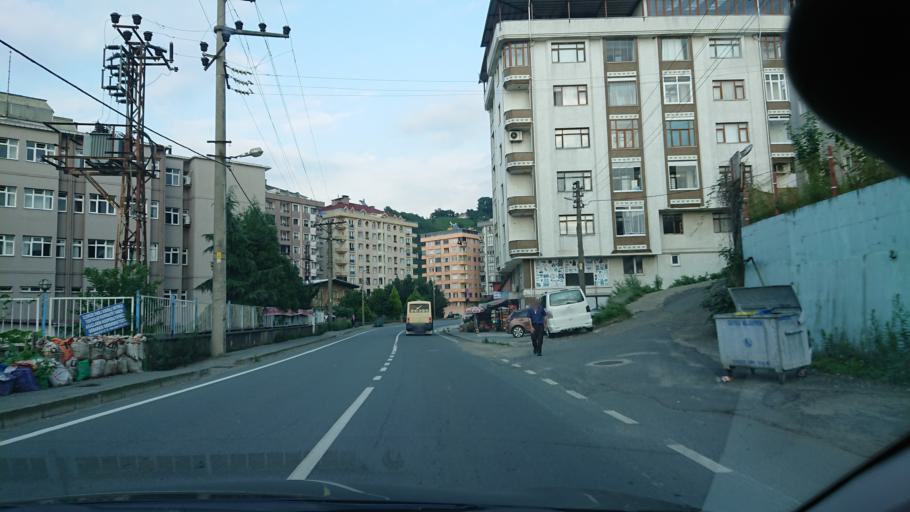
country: TR
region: Rize
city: Cayeli
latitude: 41.0823
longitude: 40.7102
